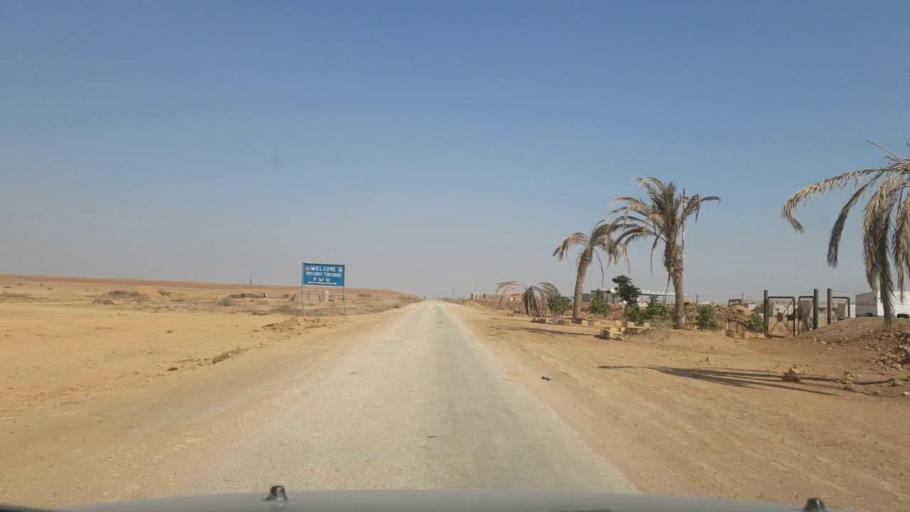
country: PK
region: Sindh
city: Thatta
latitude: 24.8859
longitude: 67.9103
